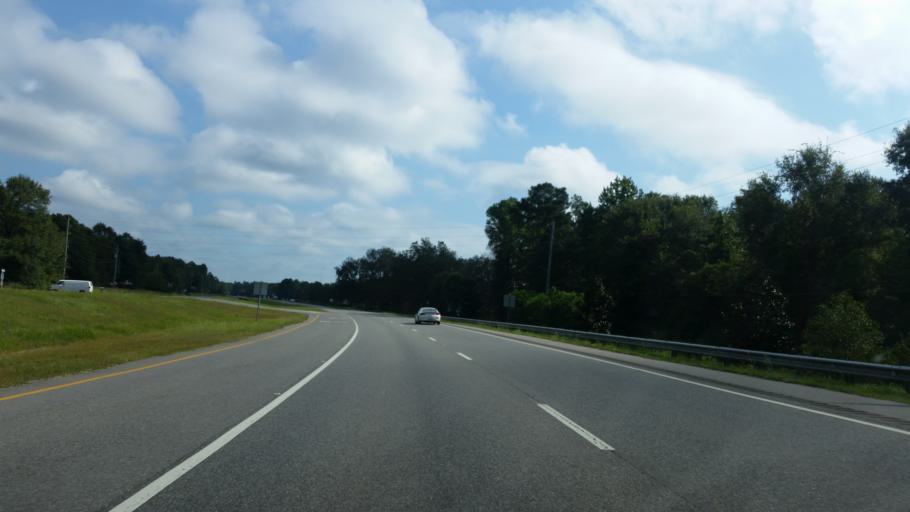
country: US
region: Alabama
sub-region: Baldwin County
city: Bay Minette
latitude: 30.9107
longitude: -87.7840
